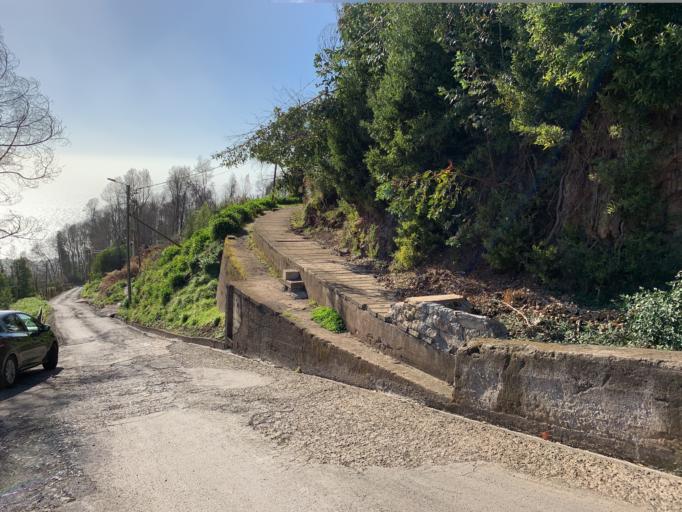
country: PT
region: Madeira
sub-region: Calheta
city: Estreito da Calheta
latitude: 32.7428
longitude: -17.1600
